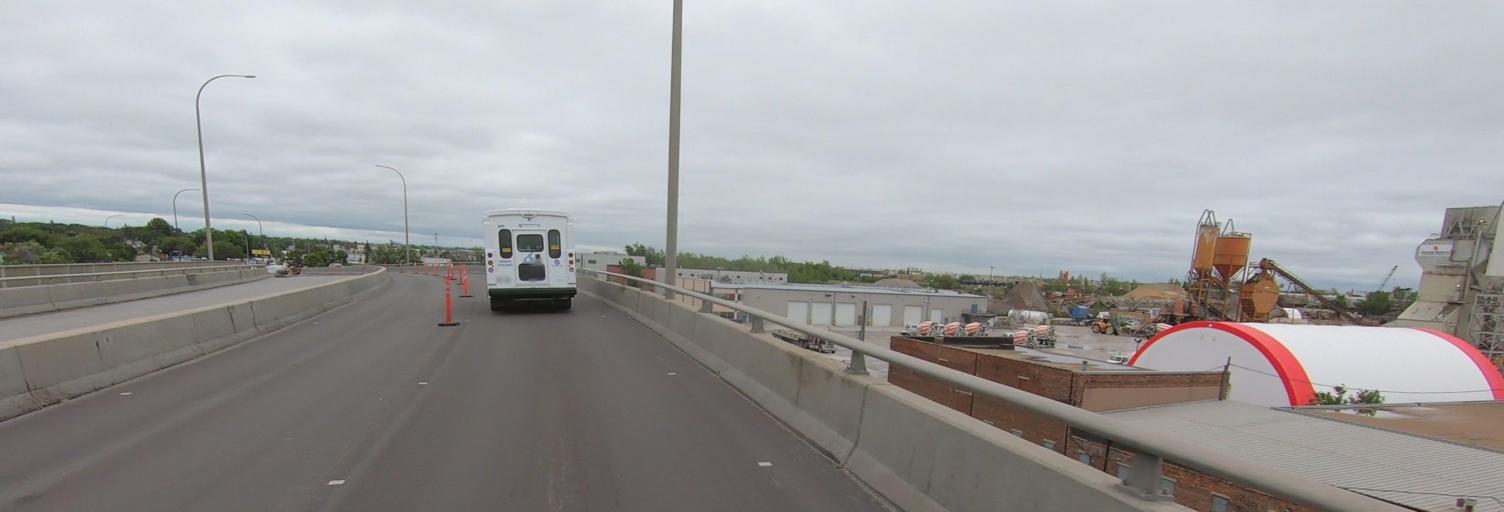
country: CA
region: Manitoba
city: Winnipeg
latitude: 49.9034
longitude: -97.1014
